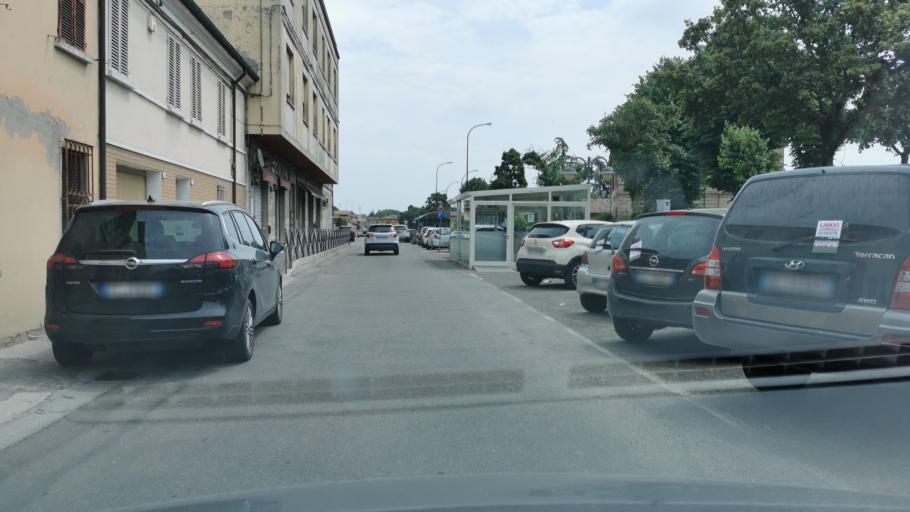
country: IT
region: Emilia-Romagna
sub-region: Provincia di Ravenna
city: Bagnacavallo
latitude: 44.4142
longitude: 11.9747
